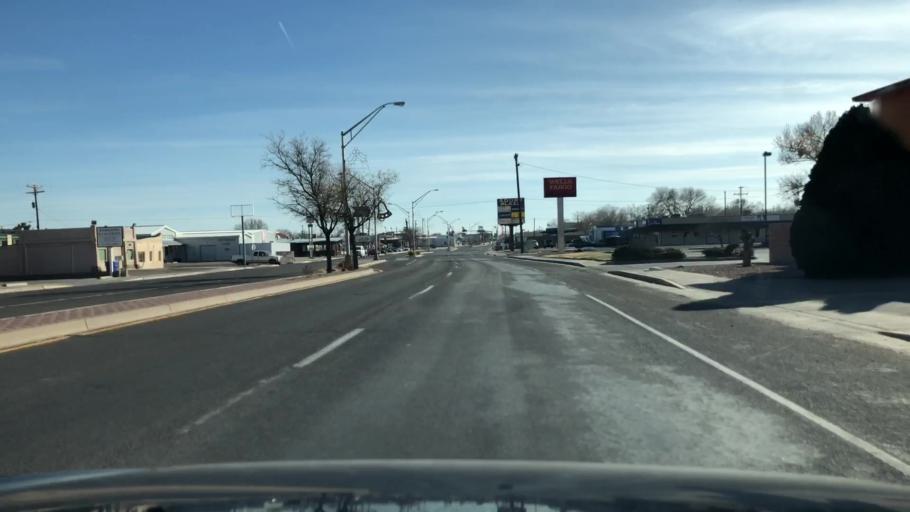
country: US
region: New Mexico
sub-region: Socorro County
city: Socorro
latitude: 34.0623
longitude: -106.8922
